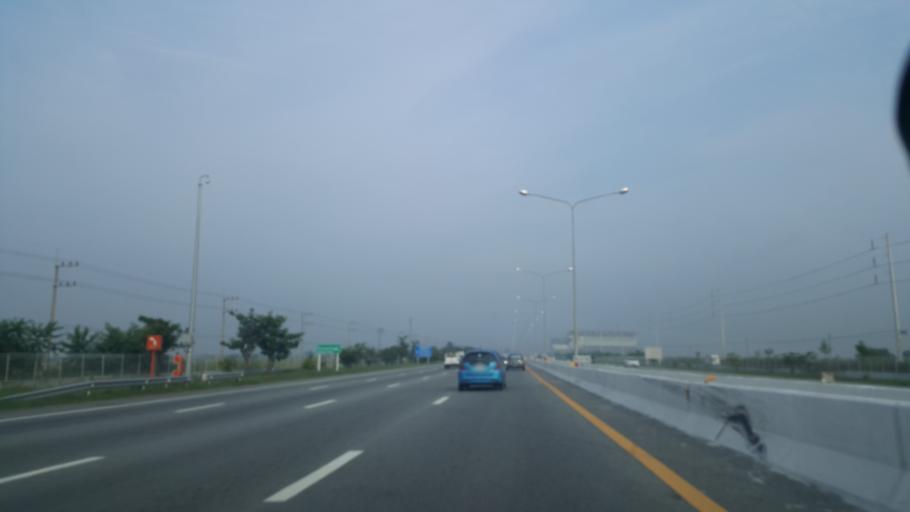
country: TH
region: Chachoengsao
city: Bang Pakong
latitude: 13.5837
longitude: 100.9715
